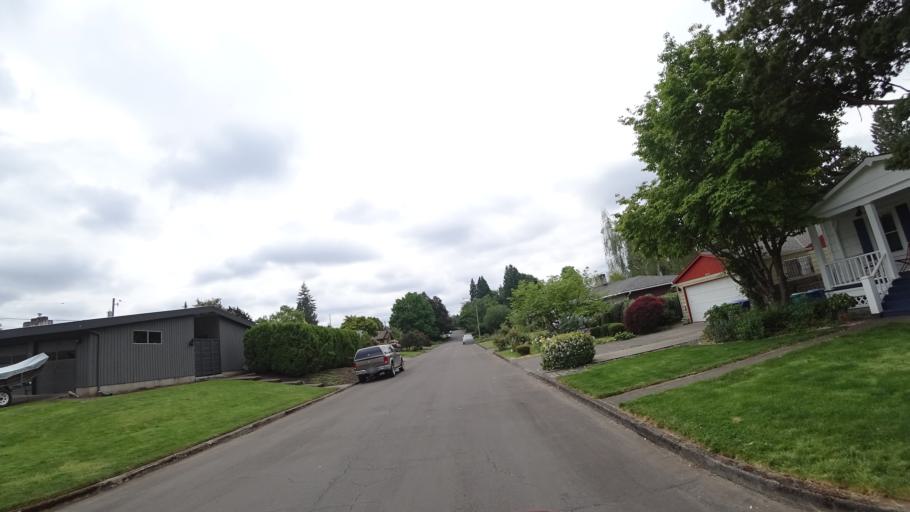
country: US
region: Oregon
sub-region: Clackamas County
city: Milwaukie
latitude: 45.4870
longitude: -122.6289
